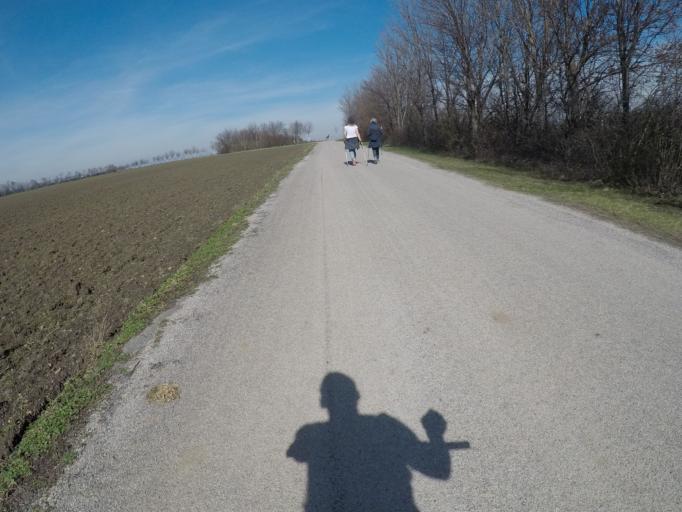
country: AT
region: Lower Austria
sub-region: Politischer Bezirk Modling
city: Biedermannsdorf
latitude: 48.1005
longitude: 16.3412
